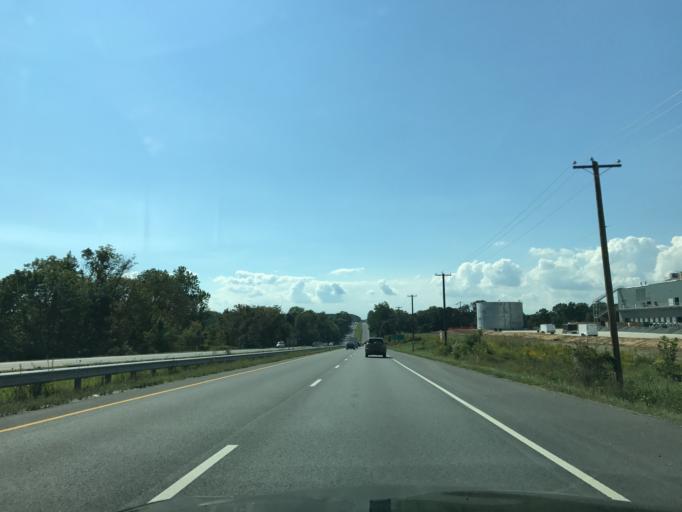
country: US
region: Maryland
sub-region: Cecil County
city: Charlestown
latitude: 39.5822
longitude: -76.0245
